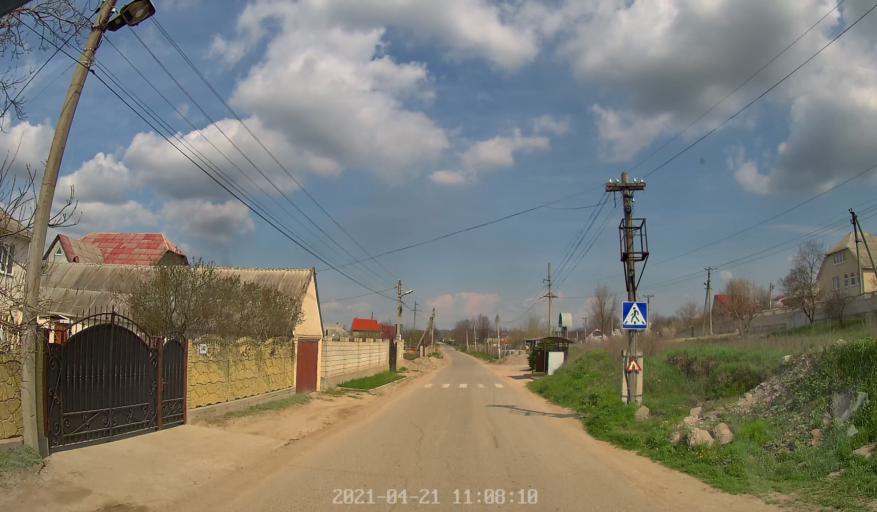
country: MD
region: Chisinau
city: Singera
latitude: 46.9530
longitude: 28.9426
